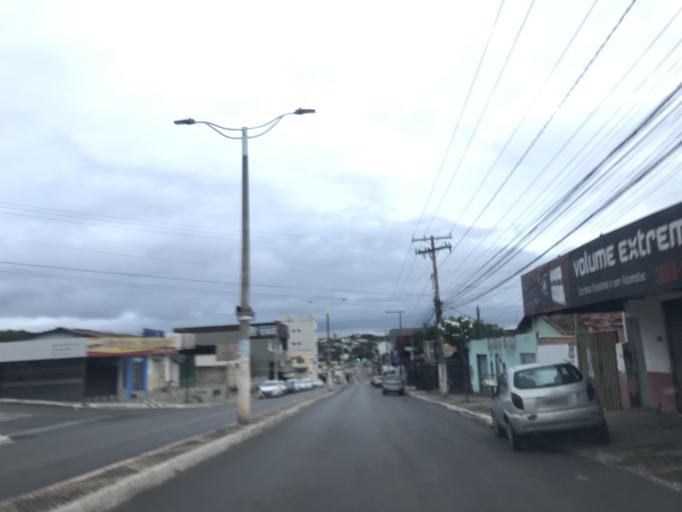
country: BR
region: Goias
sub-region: Luziania
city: Luziania
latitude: -16.2519
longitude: -47.9557
